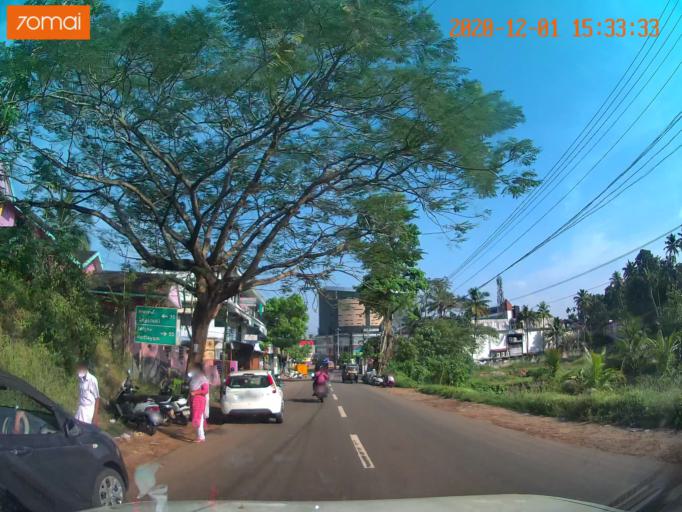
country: IN
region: Kerala
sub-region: Ernakulam
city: Muvattupuzha
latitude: 9.9763
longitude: 76.5786
